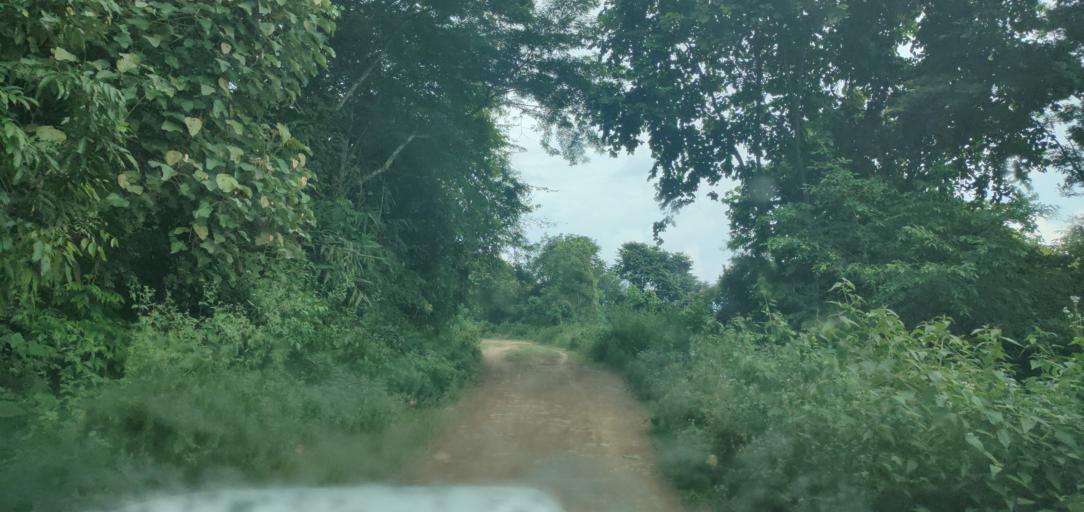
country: LA
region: Phongsali
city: Phongsali
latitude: 21.4469
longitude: 102.3147
